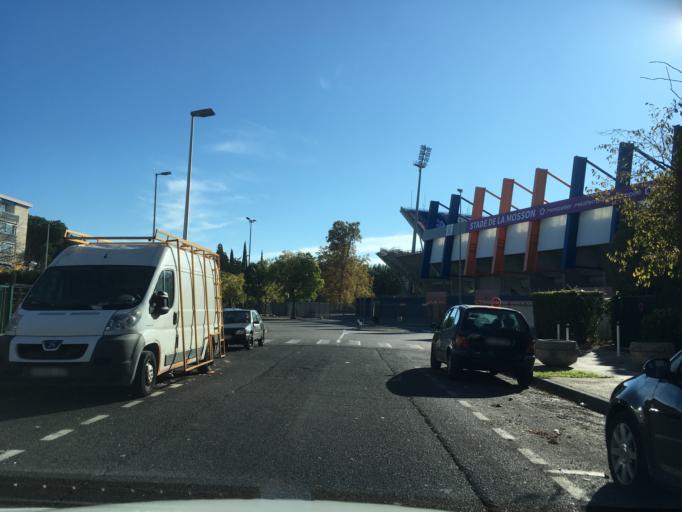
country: FR
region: Languedoc-Roussillon
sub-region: Departement de l'Herault
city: Juvignac
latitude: 43.6231
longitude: 3.8134
